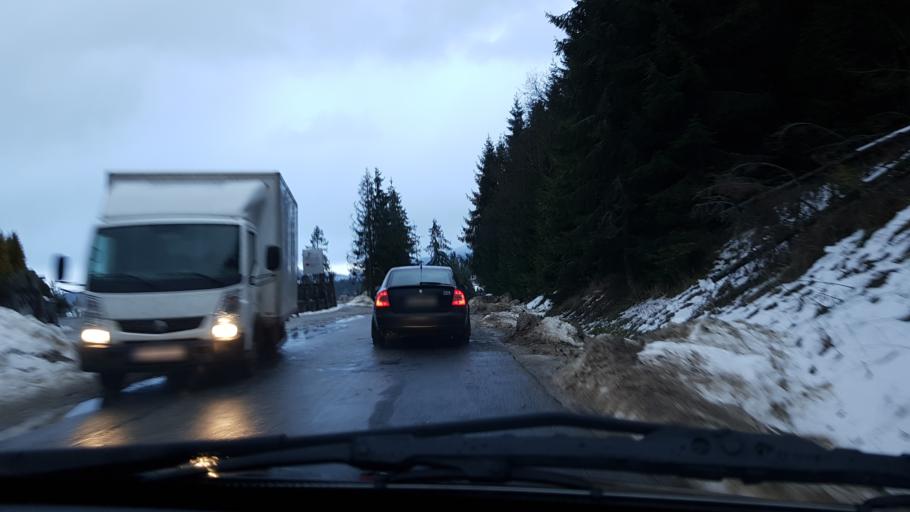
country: PL
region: Lesser Poland Voivodeship
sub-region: Powiat tatrzanski
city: Bukowina Tatrzanska
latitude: 49.3225
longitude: 20.1066
